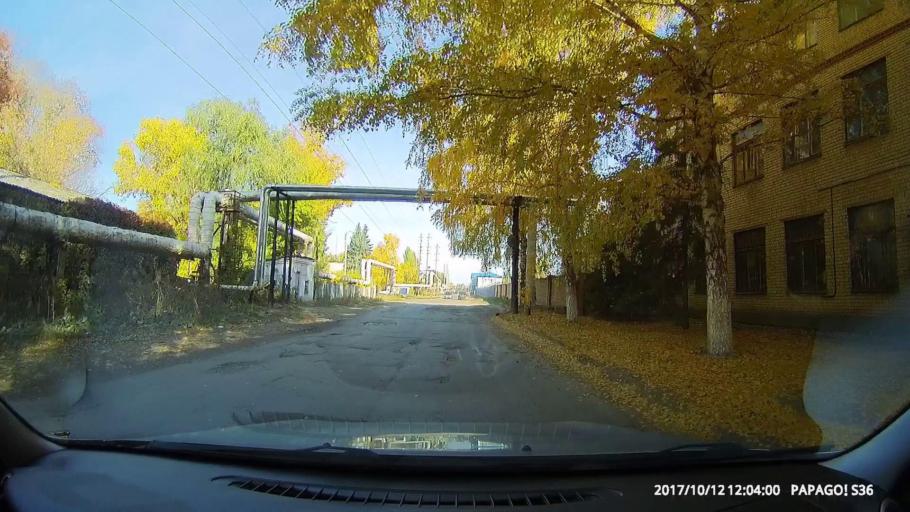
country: RU
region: Samara
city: Chapayevsk
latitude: 52.9771
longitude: 49.7171
